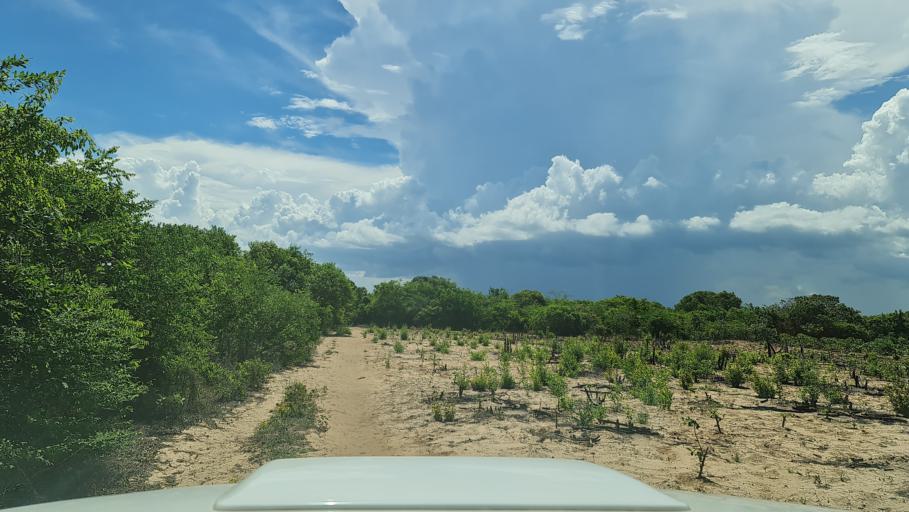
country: MZ
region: Nampula
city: Antonio Enes
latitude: -15.7072
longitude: 40.2559
